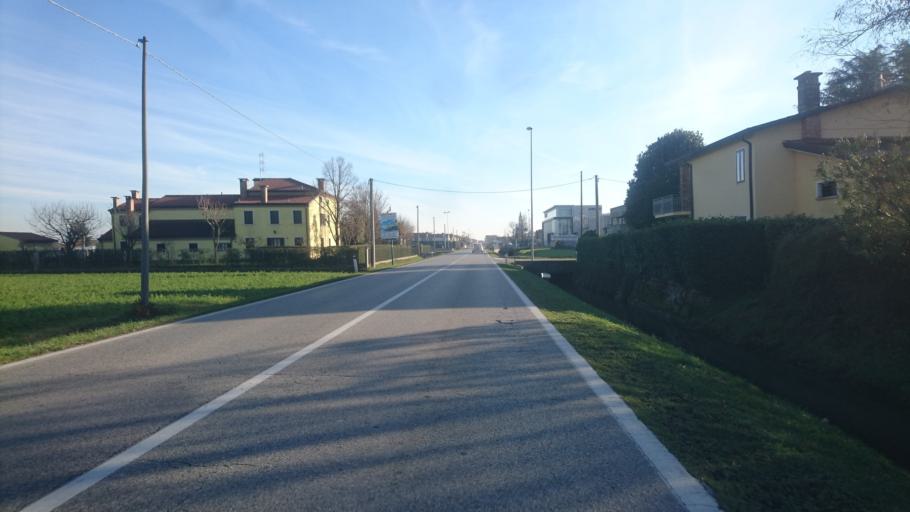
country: IT
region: Veneto
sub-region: Provincia di Padova
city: Villafranca Padovana
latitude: 45.5003
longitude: 11.7944
